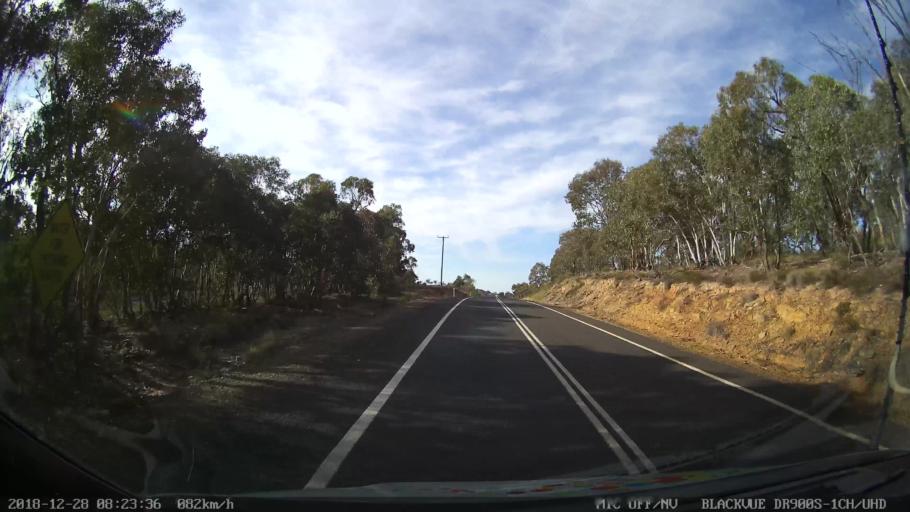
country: AU
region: New South Wales
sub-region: Blayney
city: Blayney
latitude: -33.9091
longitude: 149.3473
